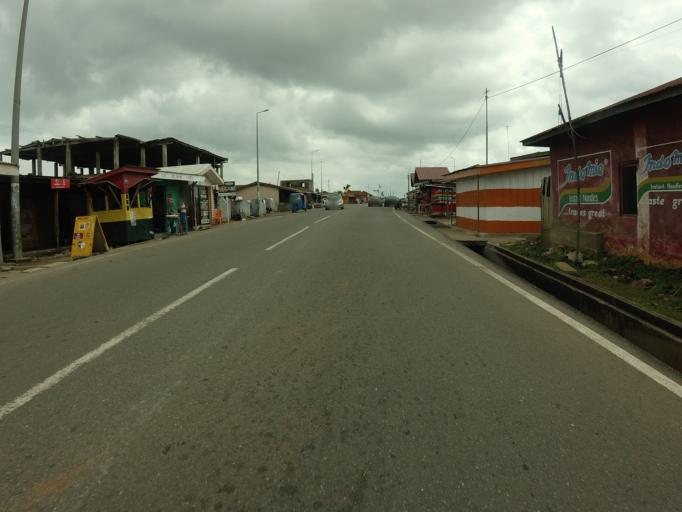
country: GH
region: Volta
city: Ho
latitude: 6.6037
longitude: 0.4711
